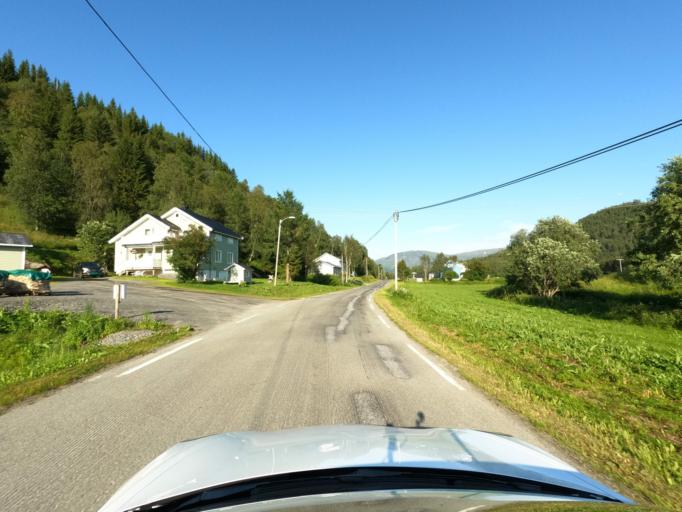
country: NO
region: Nordland
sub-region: Narvik
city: Bjerkvik
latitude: 68.5576
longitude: 17.6223
